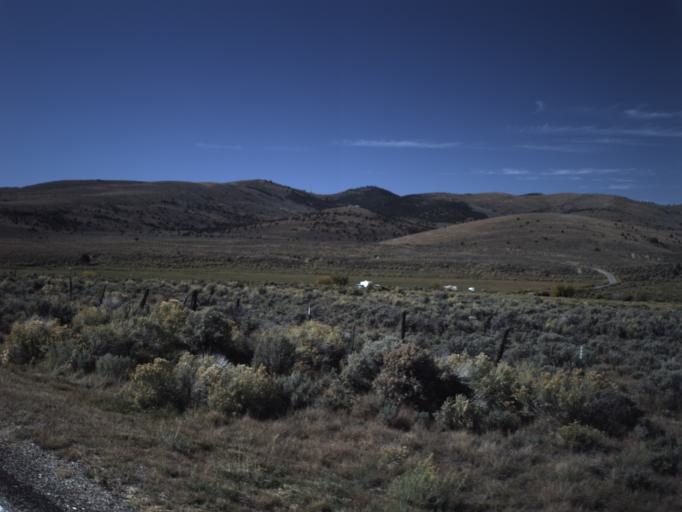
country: US
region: Utah
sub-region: Garfield County
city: Panguitch
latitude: 37.7676
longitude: -112.5460
